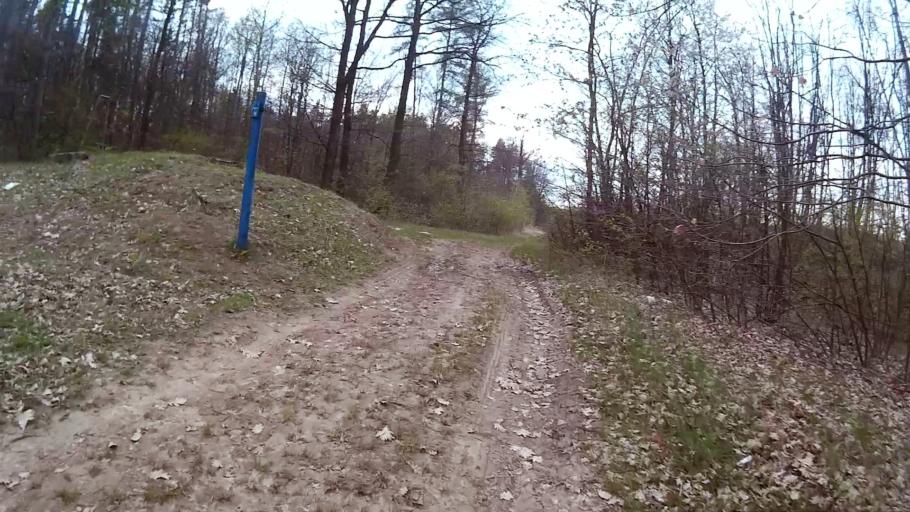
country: CZ
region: South Moravian
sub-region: Mesto Brno
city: Mokra Hora
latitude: 49.2449
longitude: 16.5417
